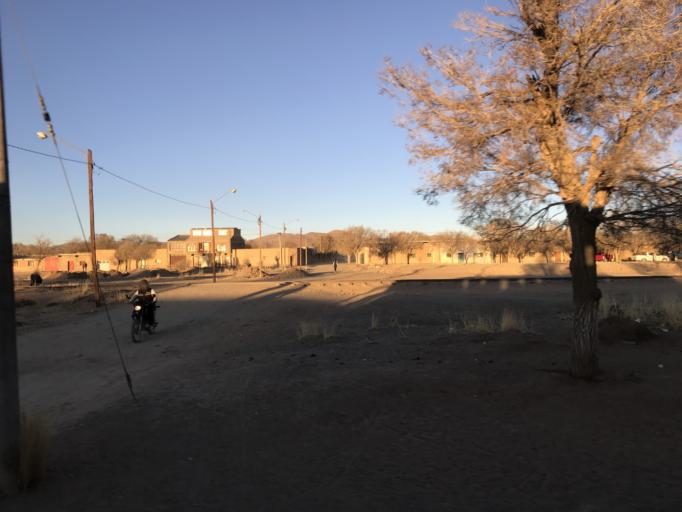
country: AR
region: Jujuy
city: Abra Pampa
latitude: -22.7204
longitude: -65.6959
